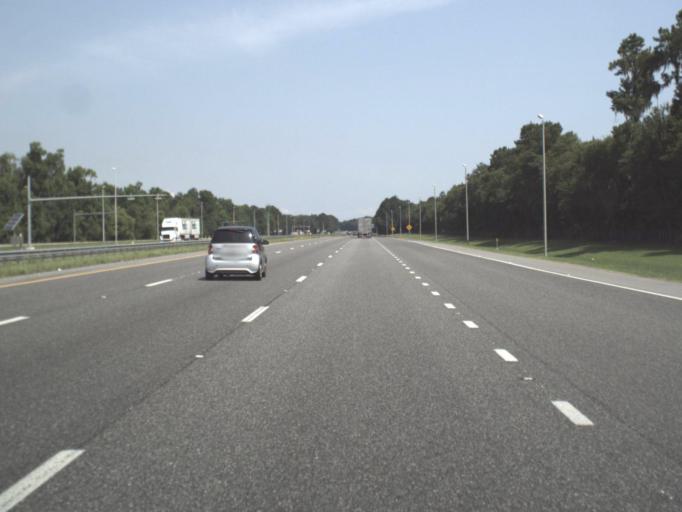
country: US
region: Florida
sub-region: Hamilton County
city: Jasper
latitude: 30.4227
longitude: -82.9029
